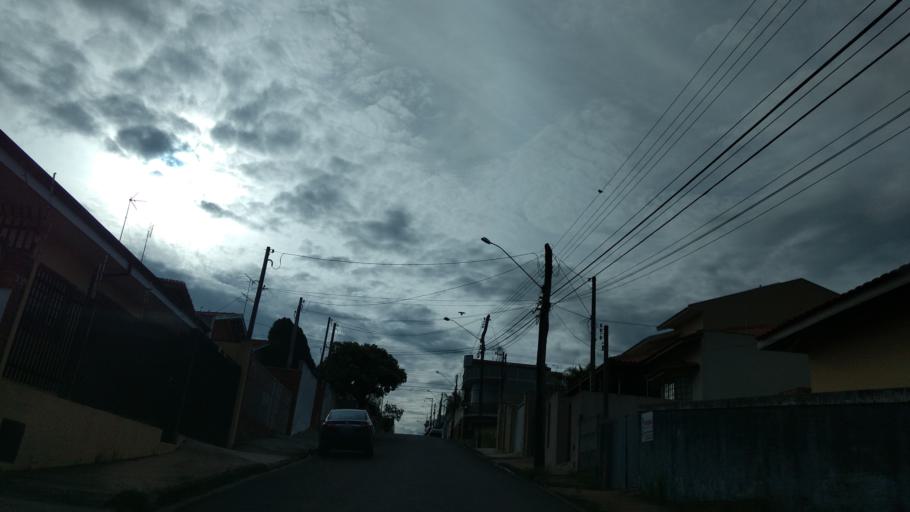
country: BR
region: Sao Paulo
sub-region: Botucatu
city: Botucatu
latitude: -22.9006
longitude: -48.4438
